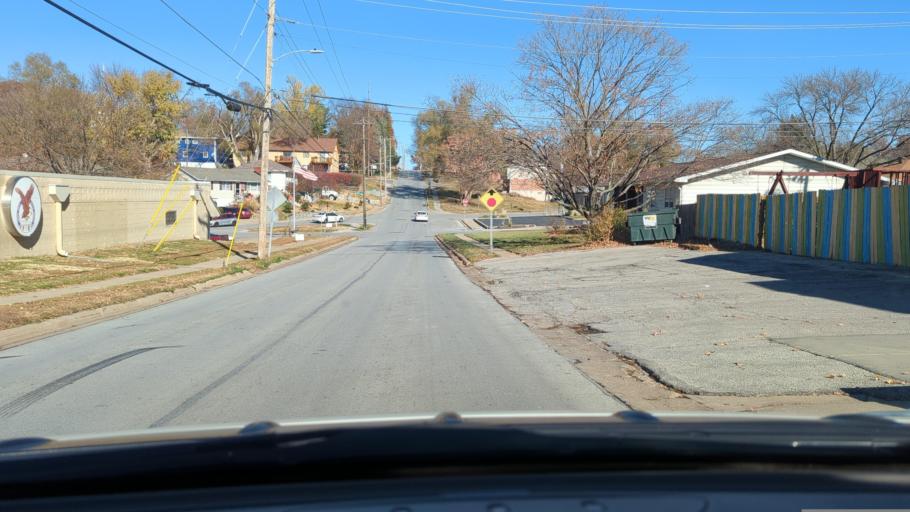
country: US
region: Nebraska
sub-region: Sarpy County
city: La Vista
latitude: 41.1928
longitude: -95.9770
